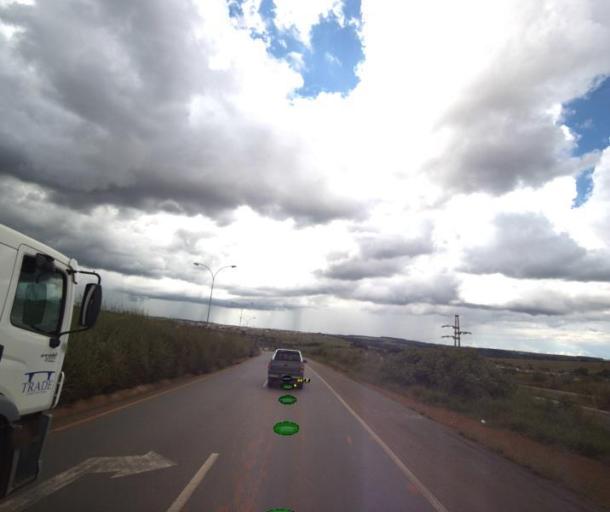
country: BR
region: Goias
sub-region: Anapolis
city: Anapolis
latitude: -16.3142
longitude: -48.9216
